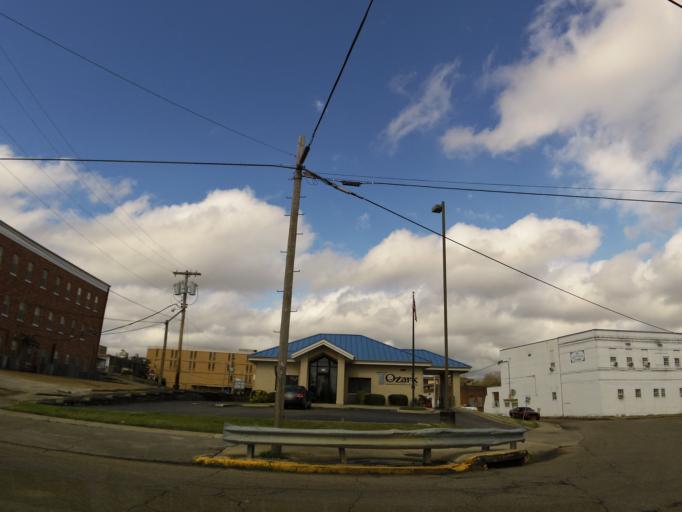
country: US
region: Missouri
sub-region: Butler County
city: Poplar Bluff
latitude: 36.7581
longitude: -90.3951
